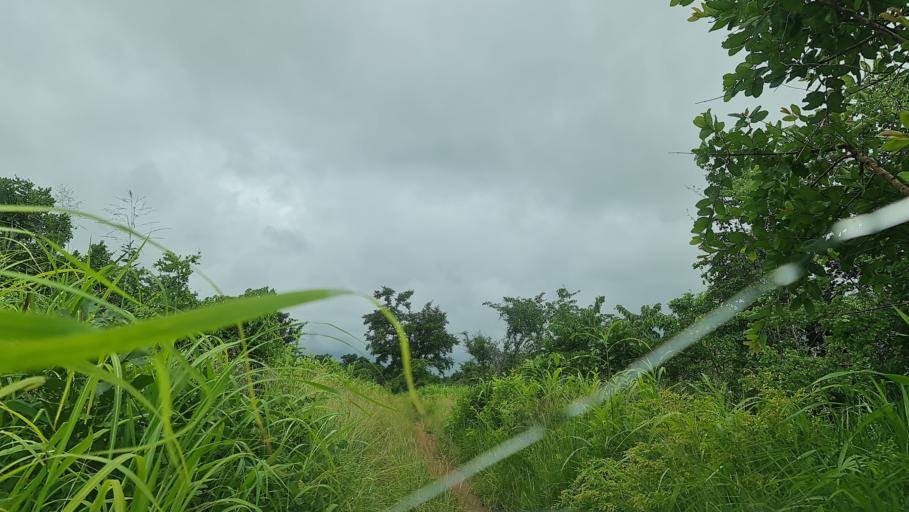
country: MW
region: Southern Region
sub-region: Nsanje District
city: Nsanje
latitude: -17.3945
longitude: 35.7854
